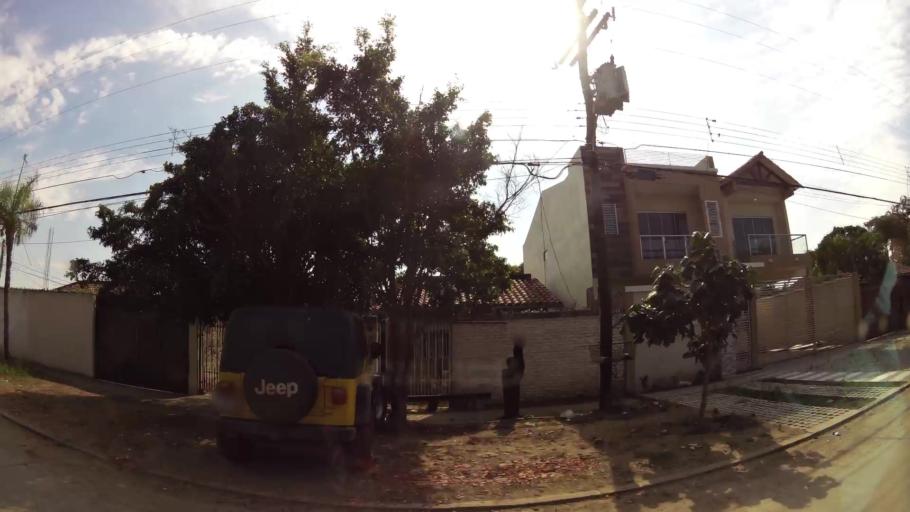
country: BO
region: Santa Cruz
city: Santa Cruz de la Sierra
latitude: -17.7286
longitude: -63.1455
